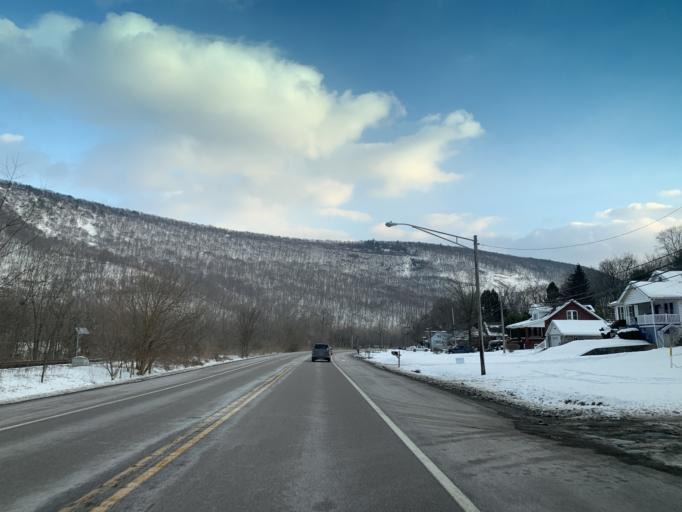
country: US
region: Maryland
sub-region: Allegany County
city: Cumberland
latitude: 39.6908
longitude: -78.7839
